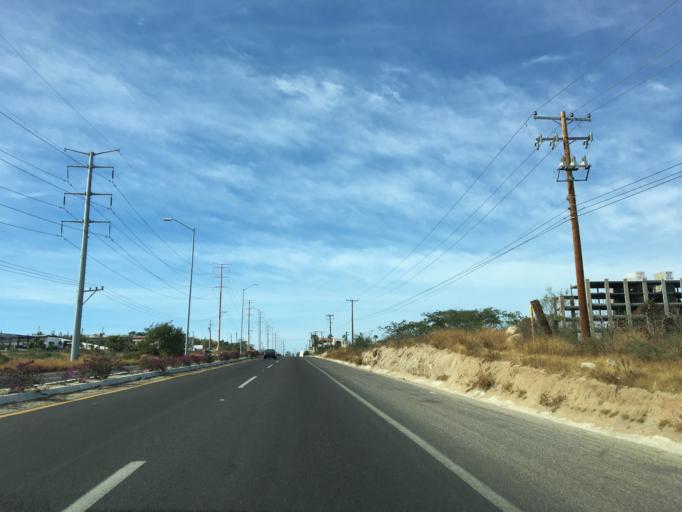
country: MX
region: Baja California Sur
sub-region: Los Cabos
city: Las Palmas
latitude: 22.9056
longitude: -109.9409
